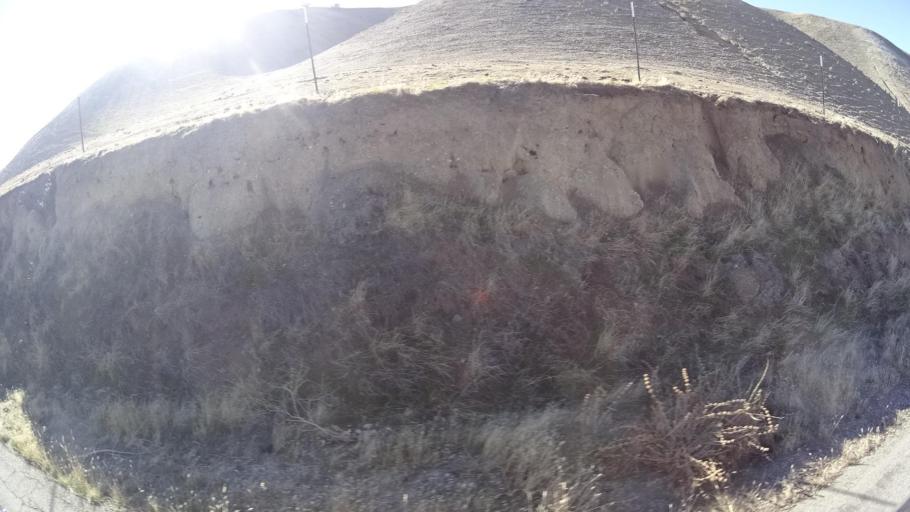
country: US
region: California
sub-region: Kern County
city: Maricopa
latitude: 34.9622
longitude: -119.4119
